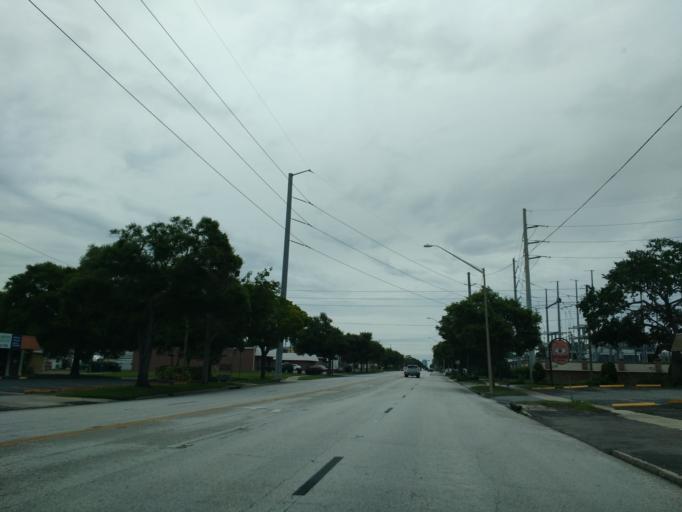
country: US
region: Florida
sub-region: Pinellas County
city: Gulfport
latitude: 27.7709
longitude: -82.7029
